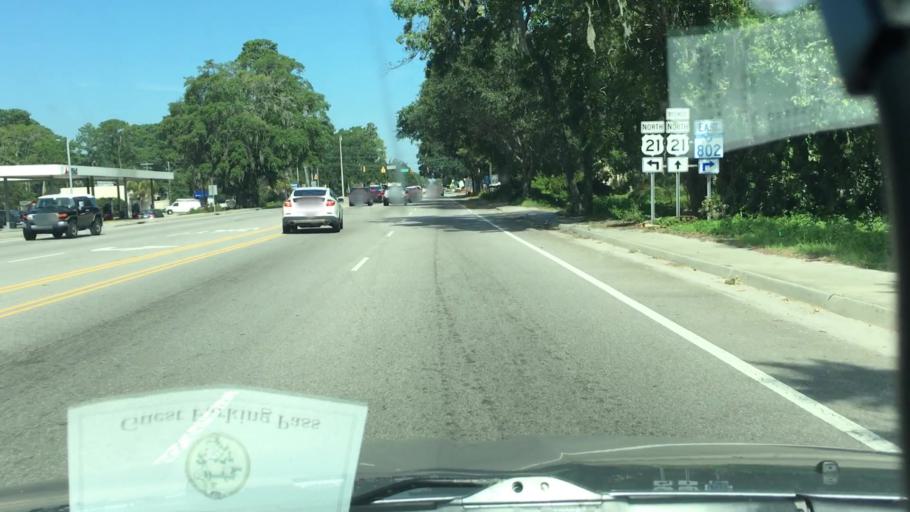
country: US
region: South Carolina
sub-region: Beaufort County
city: Beaufort
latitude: 32.4130
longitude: -80.6485
